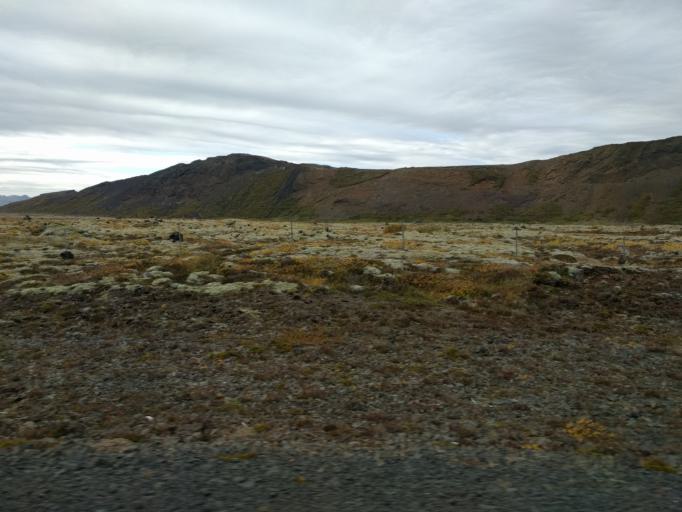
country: IS
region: South
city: Hveragerdi
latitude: 64.2206
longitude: -21.0542
